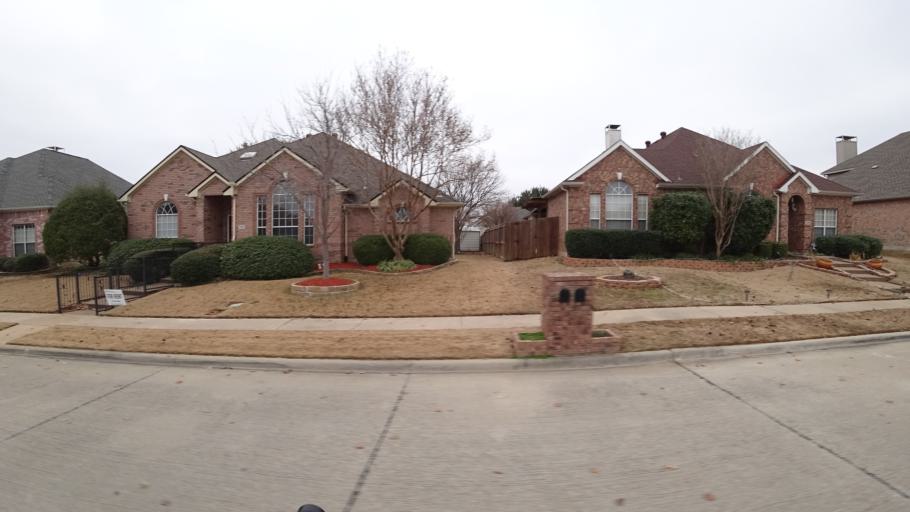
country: US
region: Texas
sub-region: Denton County
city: Highland Village
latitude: 33.0581
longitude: -97.0336
